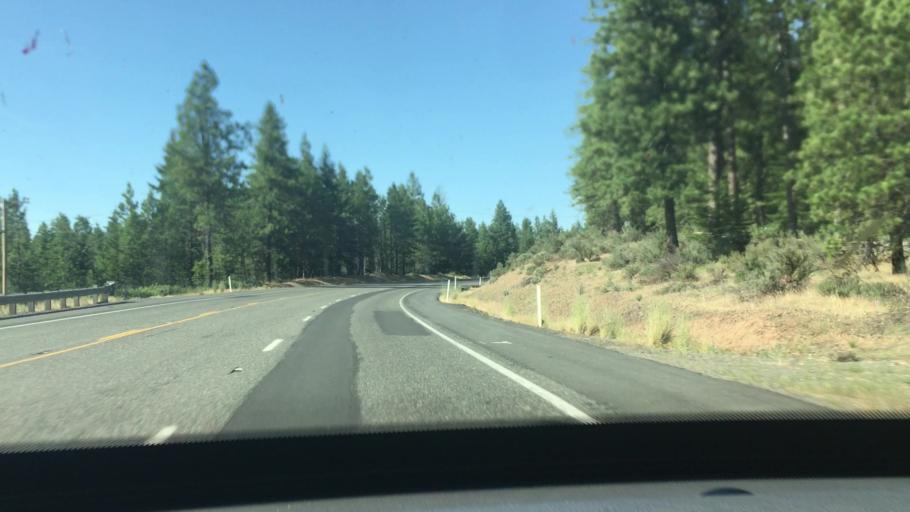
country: US
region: Washington
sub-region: Klickitat County
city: Goldendale
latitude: 45.9304
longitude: -120.6978
